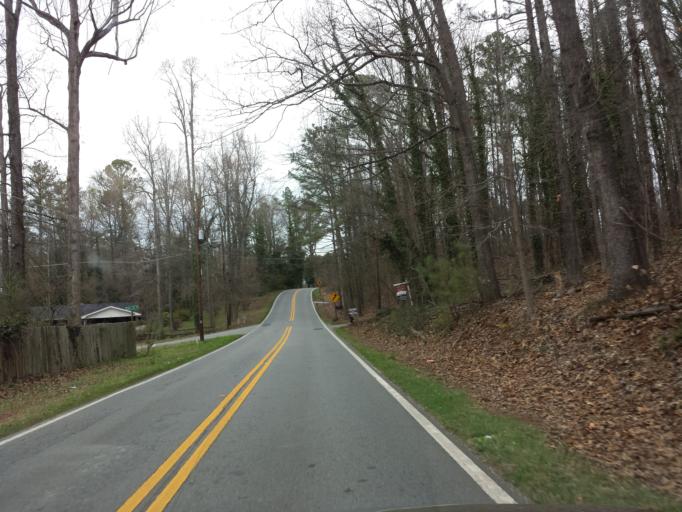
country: US
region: Georgia
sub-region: Cherokee County
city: Woodstock
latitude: 34.0340
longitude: -84.5082
